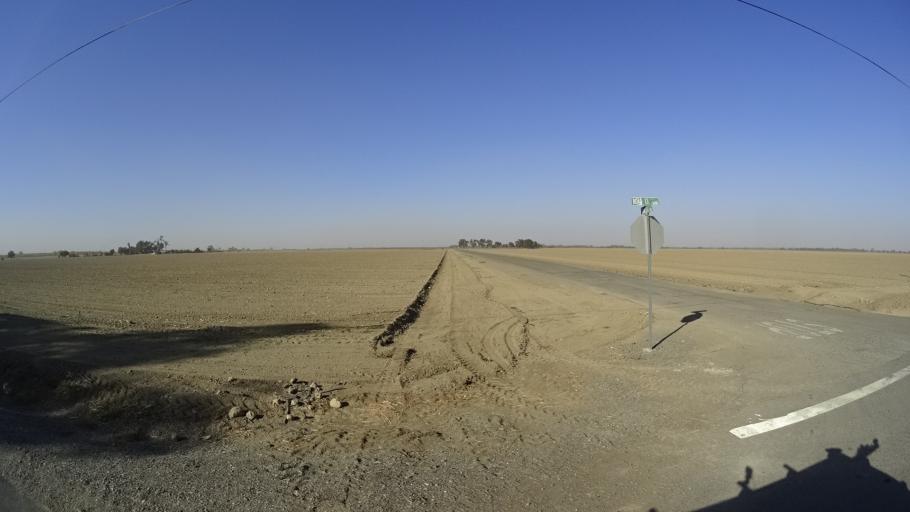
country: US
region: California
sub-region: Yolo County
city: Woodland
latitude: 38.7939
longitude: -121.8398
